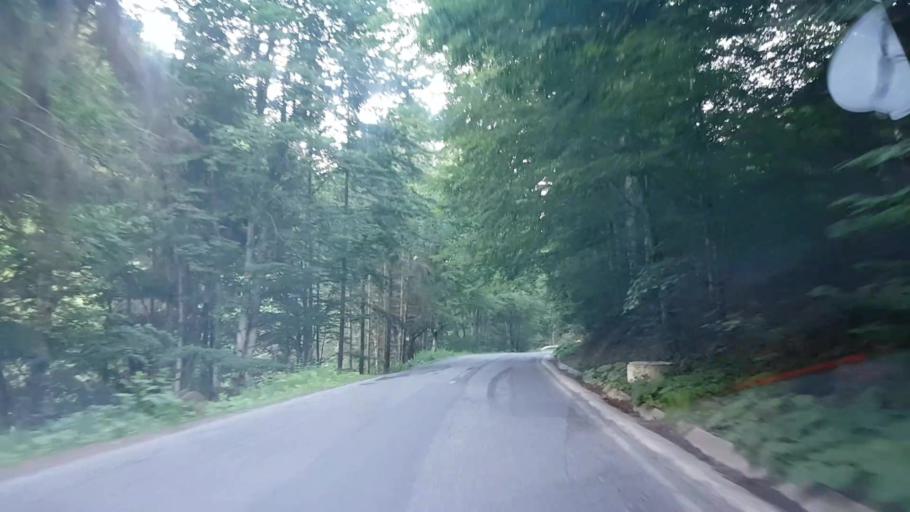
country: RO
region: Harghita
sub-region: Comuna Praid
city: Ocna de Sus
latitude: 46.6021
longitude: 25.2391
